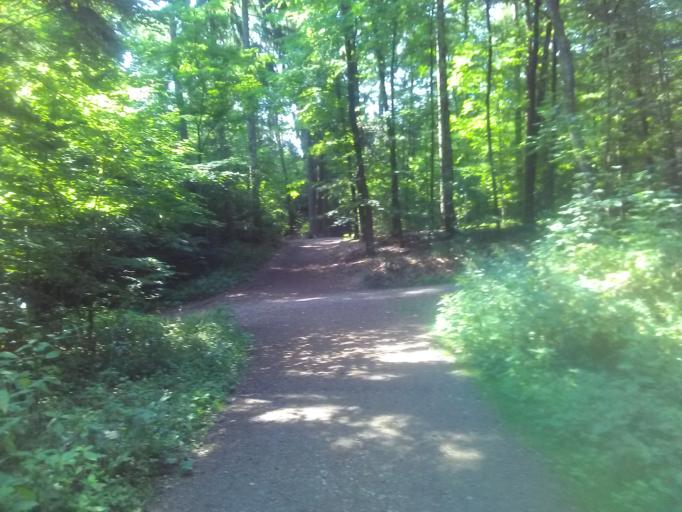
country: DE
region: Bavaria
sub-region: Upper Franconia
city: Bamberg
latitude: 49.8655
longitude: 10.8988
